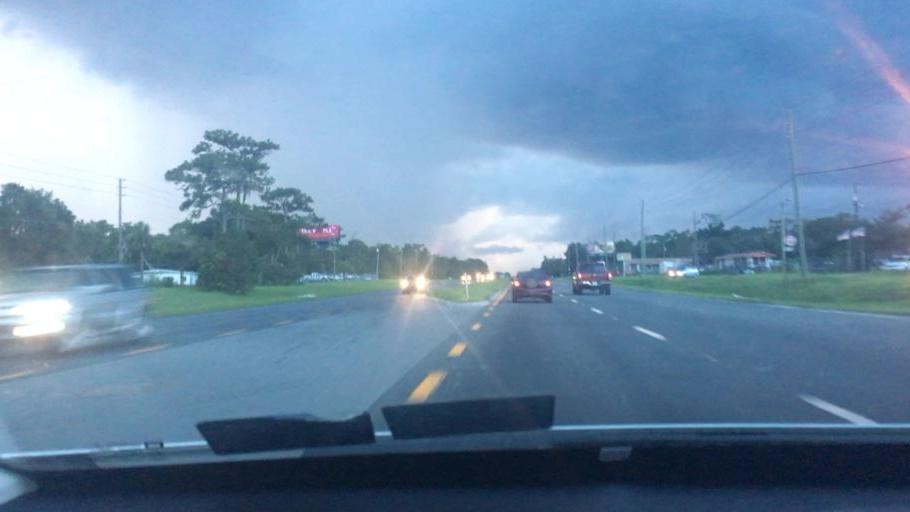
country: US
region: Florida
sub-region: Orange County
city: Bithlo
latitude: 28.5553
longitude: -81.1118
